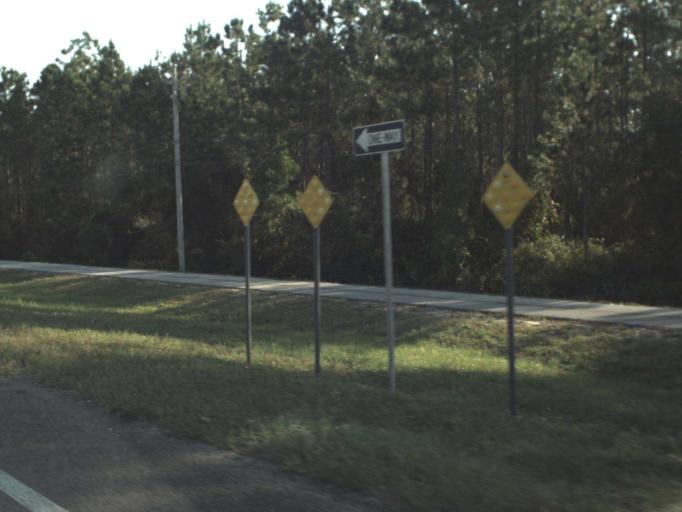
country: US
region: Florida
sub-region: Bay County
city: Laguna Beach
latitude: 30.2636
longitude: -85.8732
